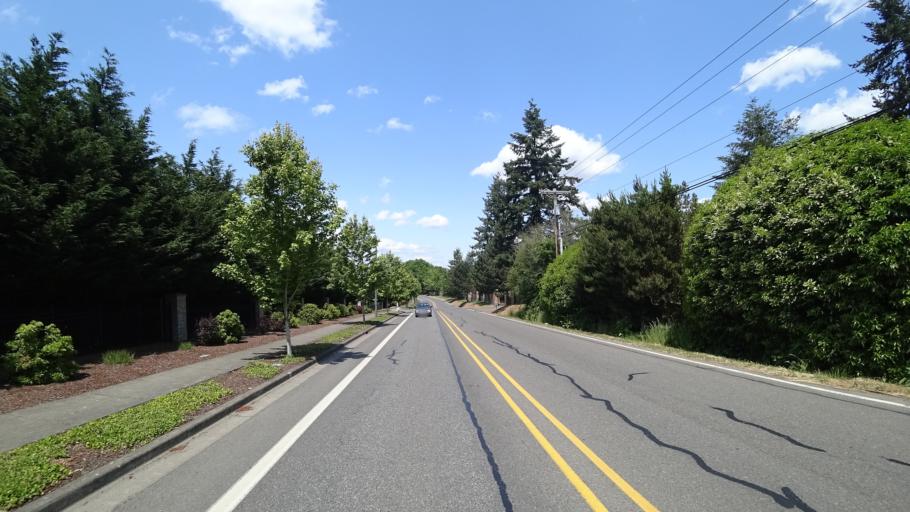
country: US
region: Oregon
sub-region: Clackamas County
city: Happy Valley
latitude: 45.4563
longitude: -122.5407
